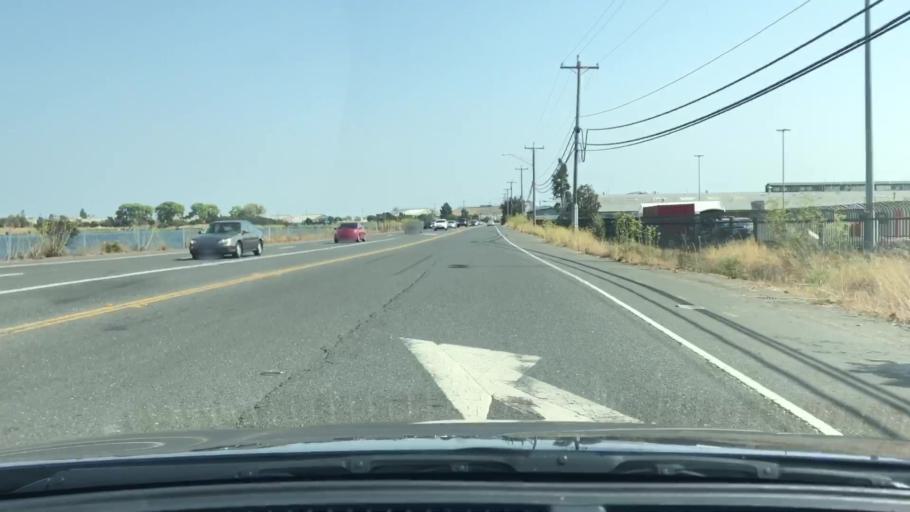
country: US
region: California
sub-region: Alameda County
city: Alameda
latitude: 37.7352
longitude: -122.2124
